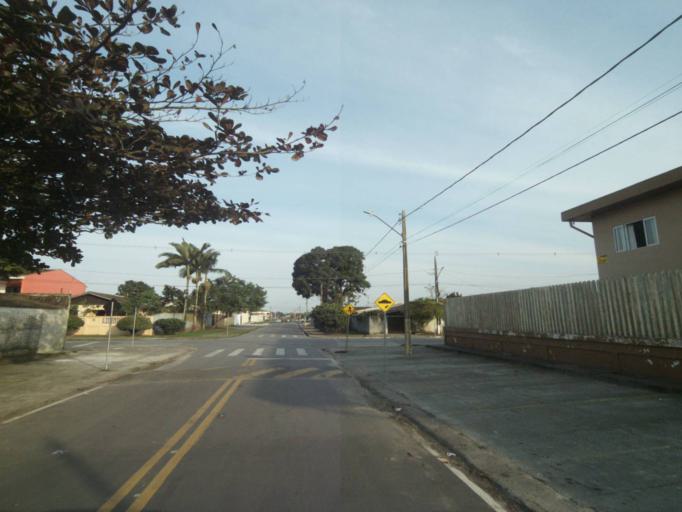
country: BR
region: Parana
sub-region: Paranagua
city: Paranagua
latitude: -25.5161
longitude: -48.5444
